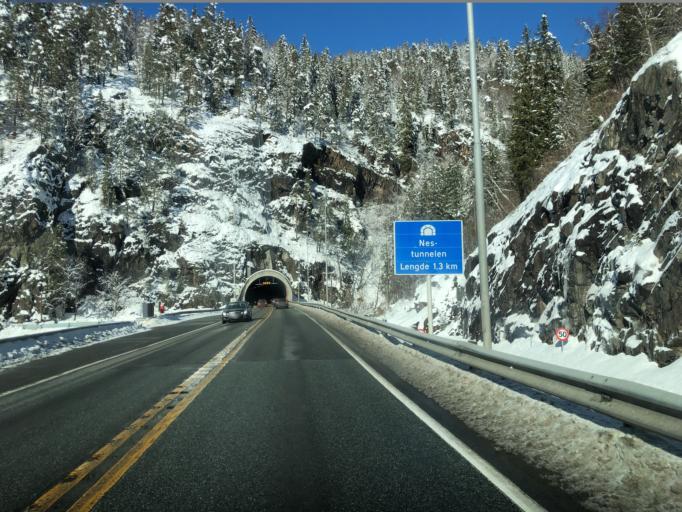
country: NO
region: Buskerud
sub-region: Hole
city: Vik
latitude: 59.9917
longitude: 10.3019
